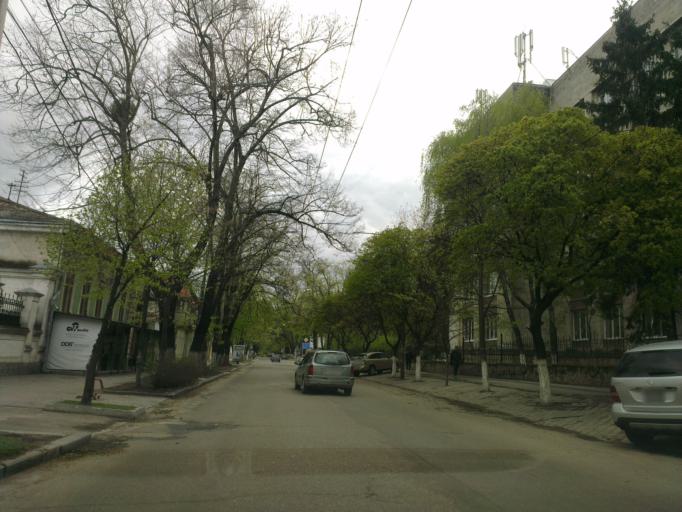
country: MD
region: Chisinau
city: Chisinau
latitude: 47.0196
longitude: 28.8250
